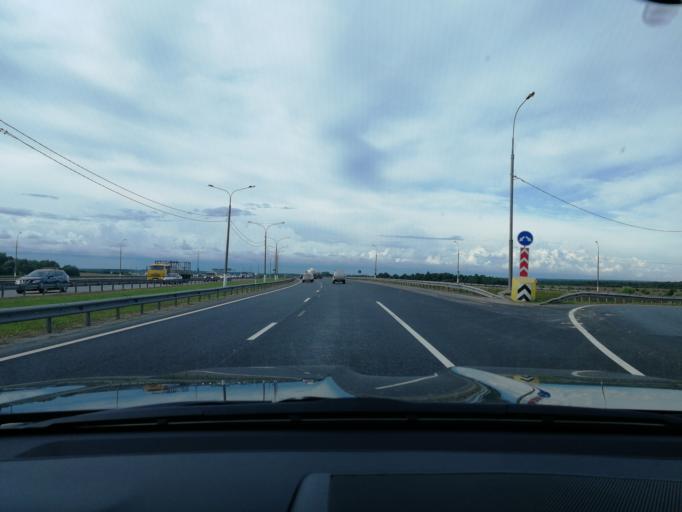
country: RU
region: Moskovskaya
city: Mikhnevo
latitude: 55.0773
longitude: 37.9365
